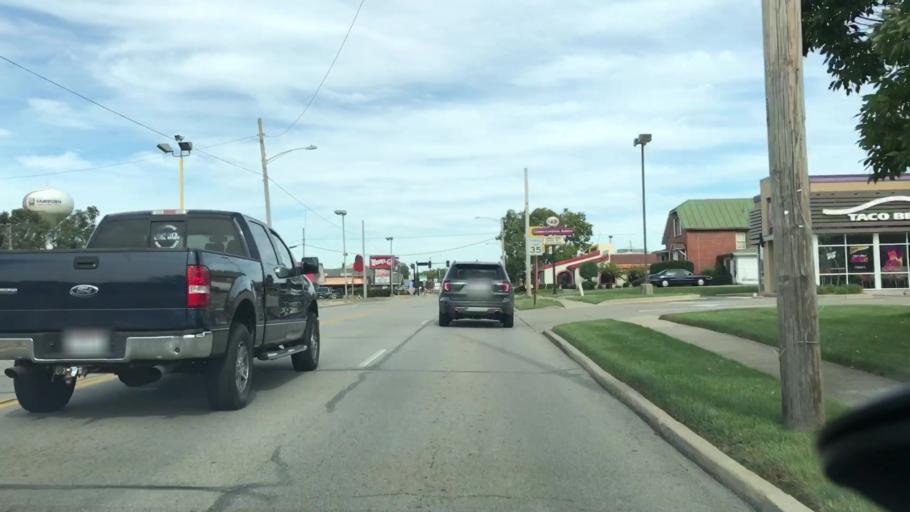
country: US
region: Ohio
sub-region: Greene County
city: Fairborn
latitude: 39.8277
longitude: -84.0263
